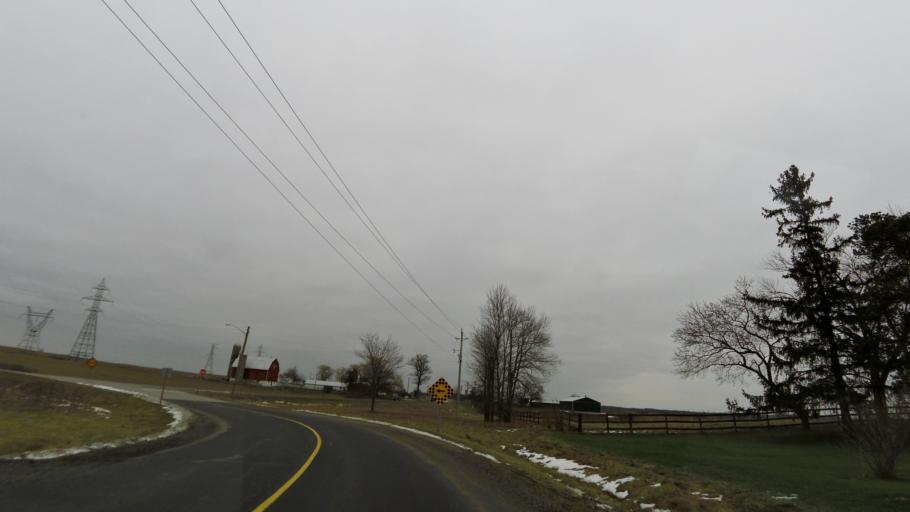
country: CA
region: Ontario
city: Brantford
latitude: 43.1084
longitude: -80.1779
